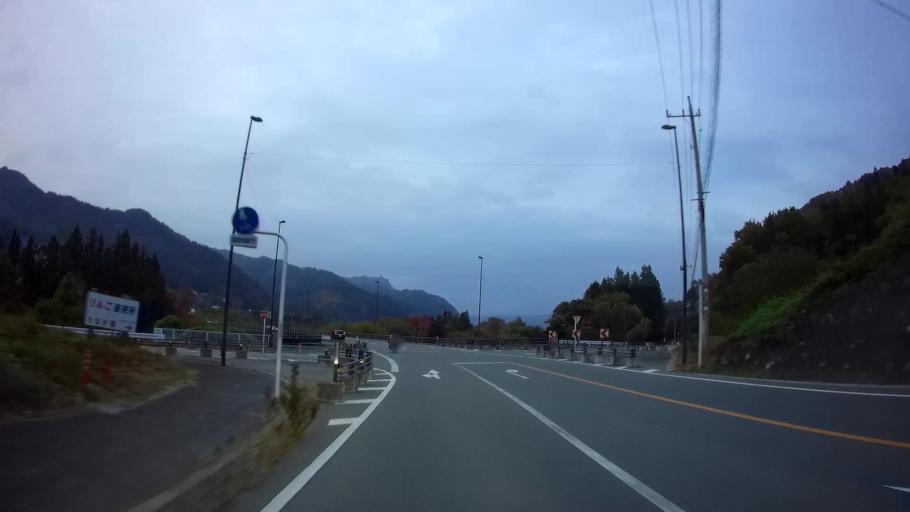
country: JP
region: Gunma
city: Nakanojomachi
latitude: 36.5602
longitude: 138.7561
